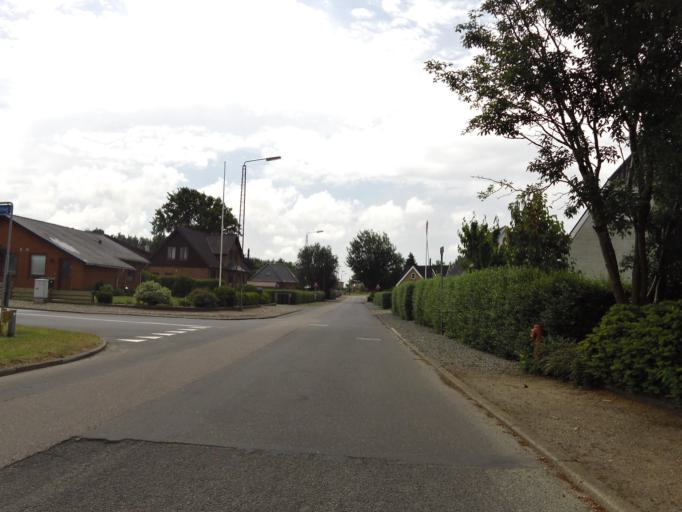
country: DK
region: South Denmark
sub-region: Tonder Kommune
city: Sherrebek
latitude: 55.1619
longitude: 8.7721
